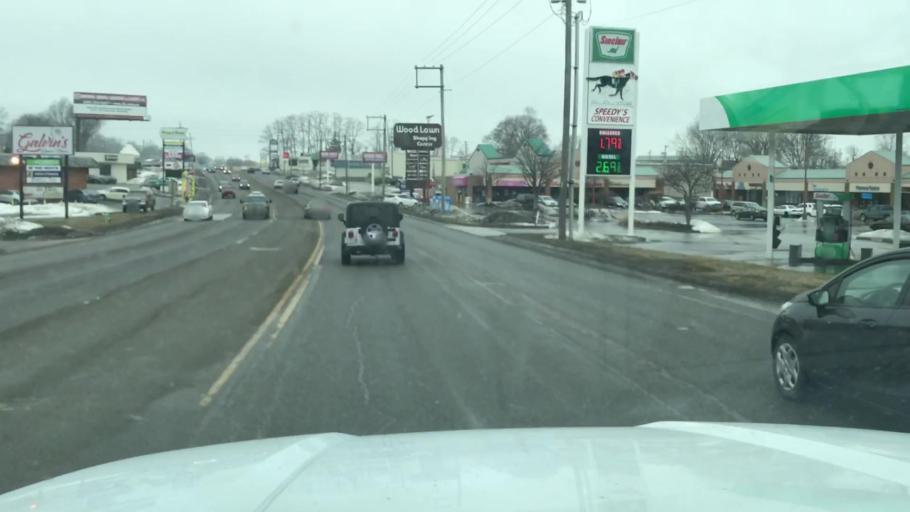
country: US
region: Missouri
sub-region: Buchanan County
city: Saint Joseph
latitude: 39.7862
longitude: -94.8043
